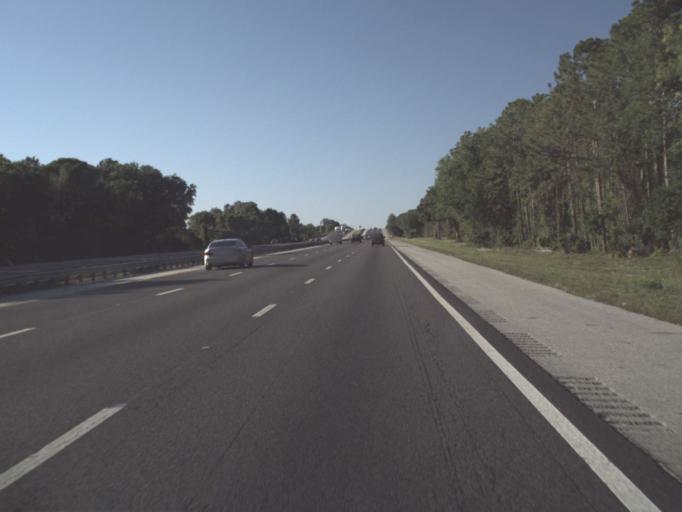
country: US
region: Florida
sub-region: Flagler County
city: Flagler Beach
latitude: 29.4892
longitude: -81.1887
